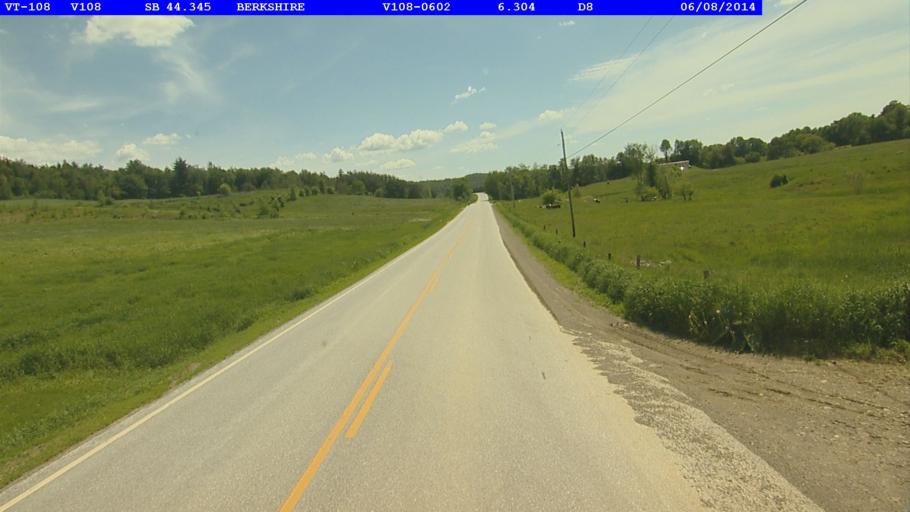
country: US
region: Vermont
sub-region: Franklin County
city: Enosburg Falls
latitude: 45.0078
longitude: -72.8245
